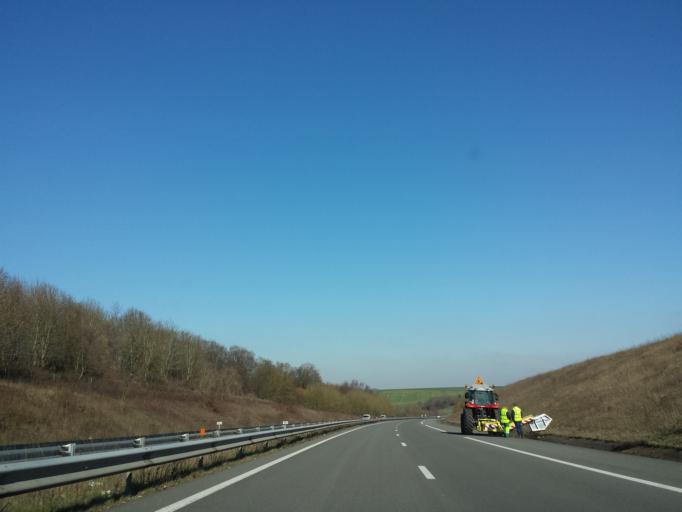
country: FR
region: Picardie
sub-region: Departement de l'Oise
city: Breteuil
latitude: 49.6671
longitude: 2.2084
